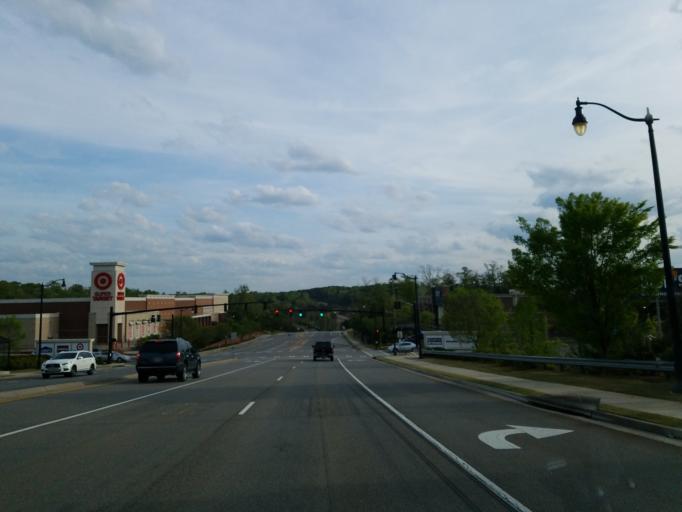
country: US
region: Georgia
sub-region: Cherokee County
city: Canton
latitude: 34.2357
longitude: -84.4580
